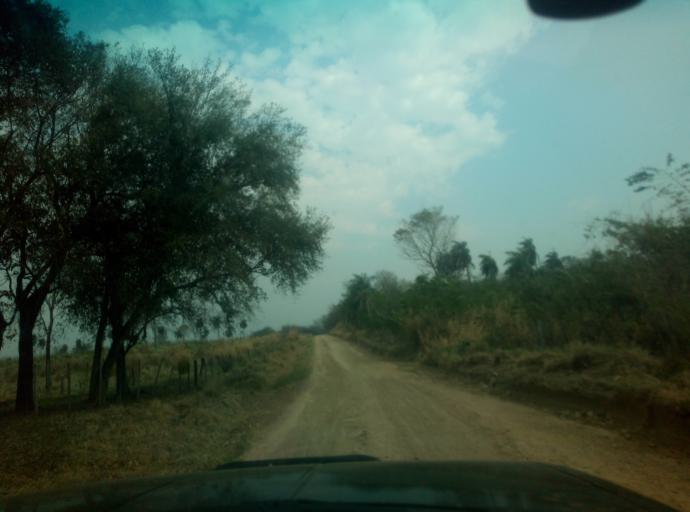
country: PY
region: Caaguazu
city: San Joaquin
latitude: -25.0855
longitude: -56.1431
